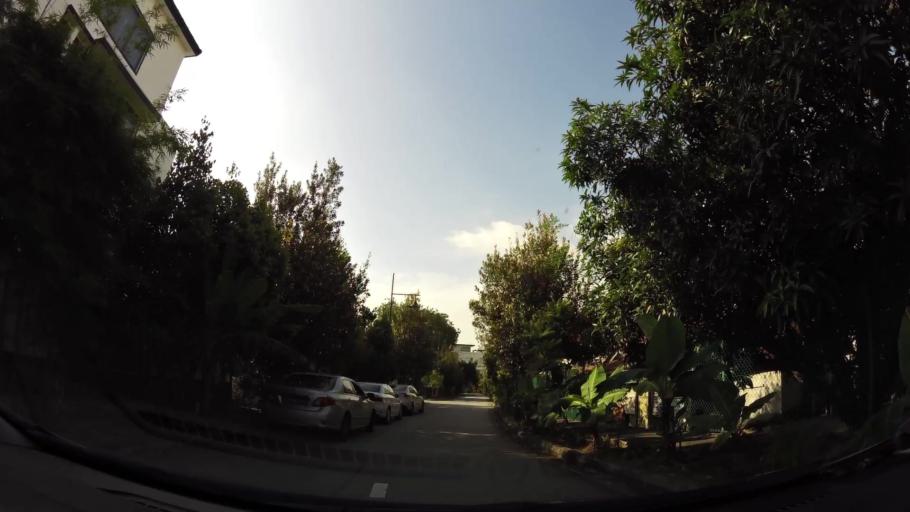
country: SG
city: Singapore
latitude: 1.3168
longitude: 103.9300
